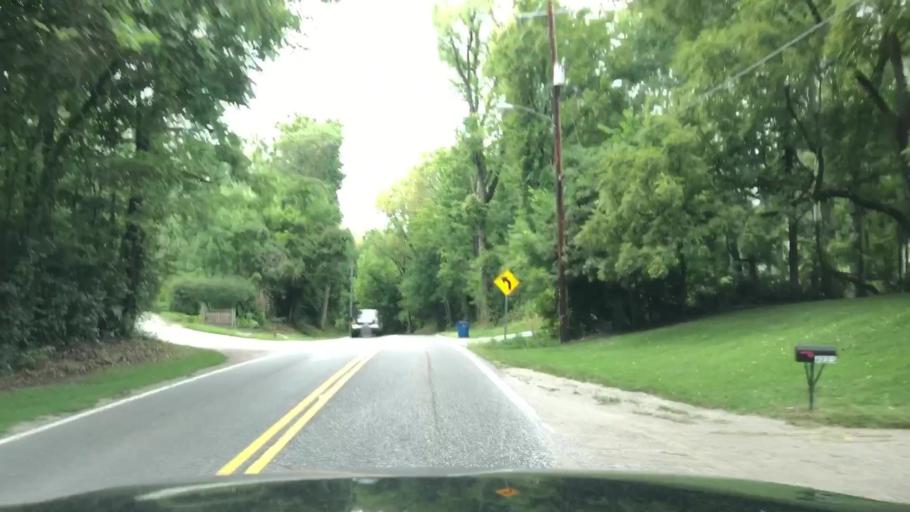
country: US
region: Missouri
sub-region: Saint Louis County
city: Hazelwood
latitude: 38.8100
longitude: -90.3854
